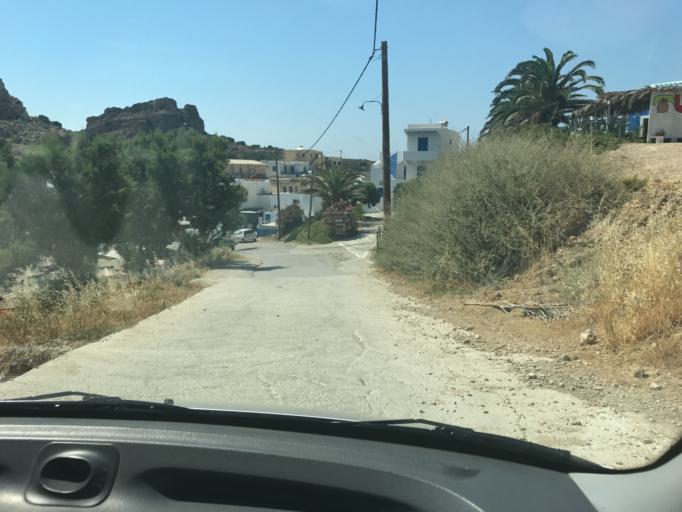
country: GR
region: South Aegean
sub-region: Nomos Dodekanisou
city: Karpathos
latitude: 35.4918
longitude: 27.1178
